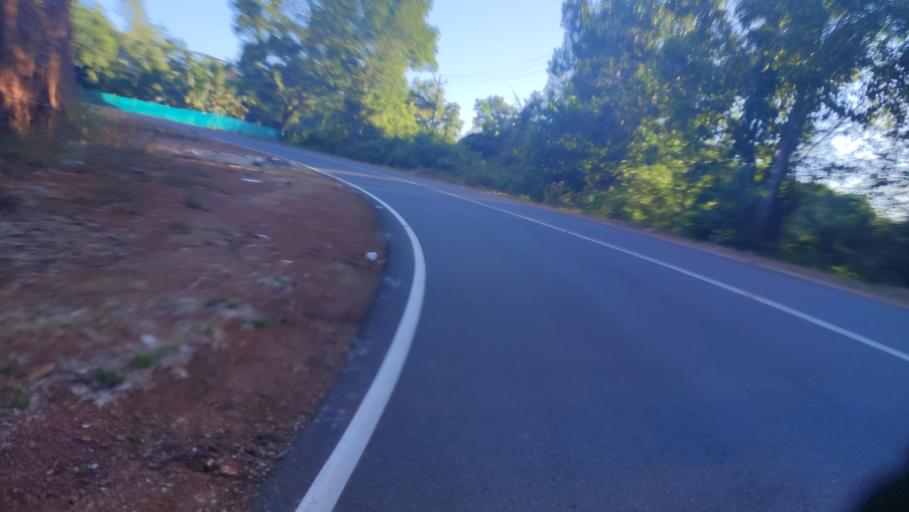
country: IN
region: Kerala
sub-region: Kasaragod District
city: Kasaragod
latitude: 12.4584
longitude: 75.0885
